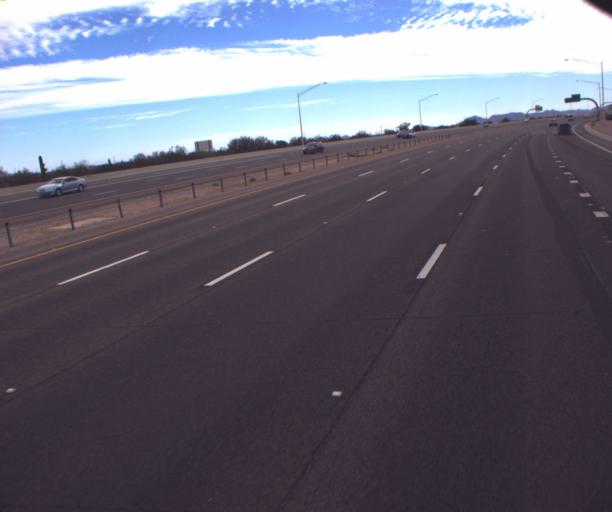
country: US
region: Arizona
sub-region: Maricopa County
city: Queen Creek
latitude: 33.3432
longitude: -111.6440
